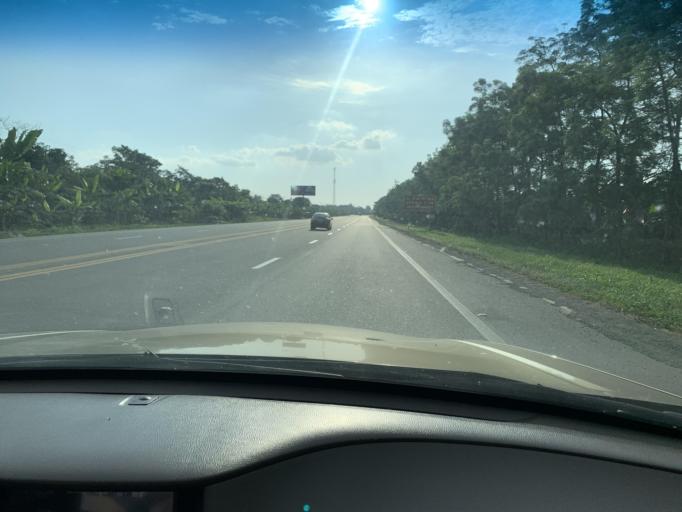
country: EC
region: Guayas
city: Coronel Marcelino Mariduena
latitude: -2.2797
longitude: -79.5242
